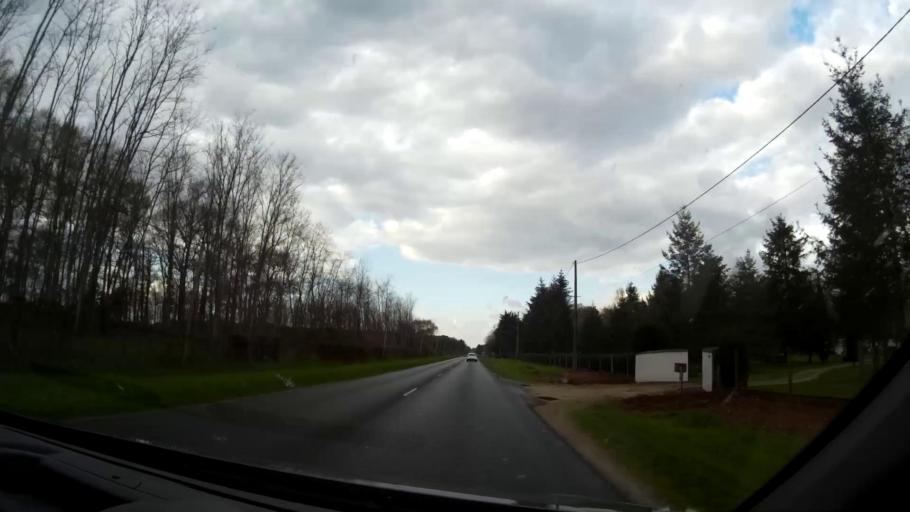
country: FR
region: Centre
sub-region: Departement du Loir-et-Cher
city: Contres
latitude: 47.4456
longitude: 1.4264
